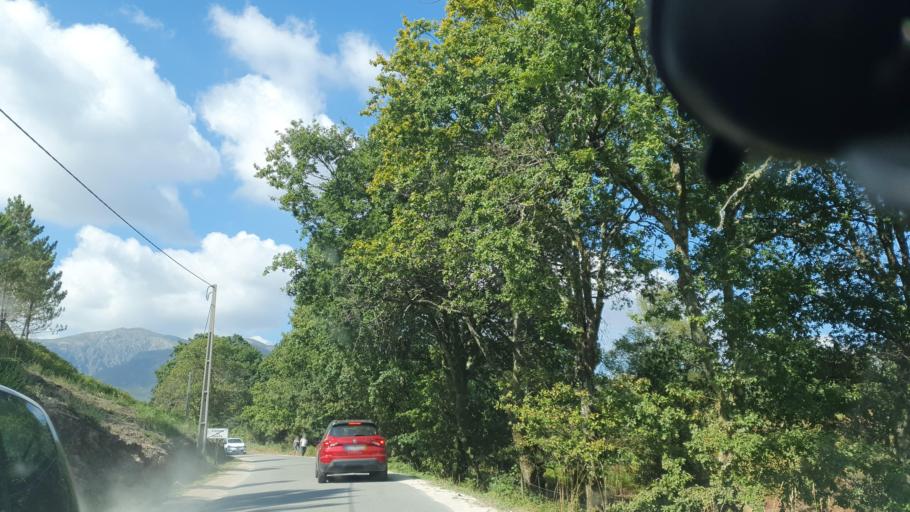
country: PT
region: Braga
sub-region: Terras de Bouro
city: Antas
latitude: 41.7658
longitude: -8.1900
